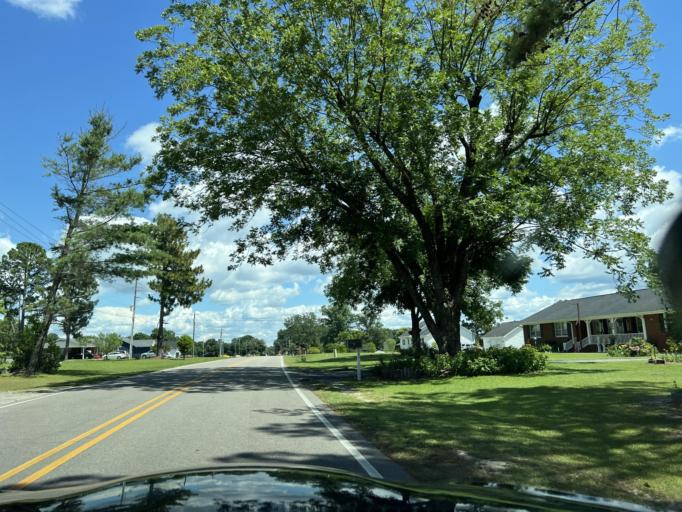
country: US
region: North Carolina
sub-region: Lee County
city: Sanford
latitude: 35.4375
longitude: -79.1698
